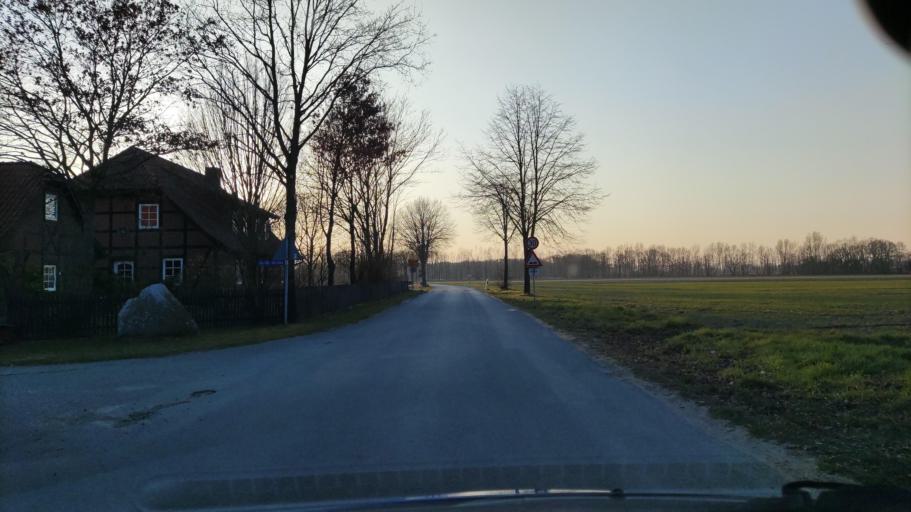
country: DE
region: Lower Saxony
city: Dannenberg
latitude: 53.1111
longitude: 11.1274
